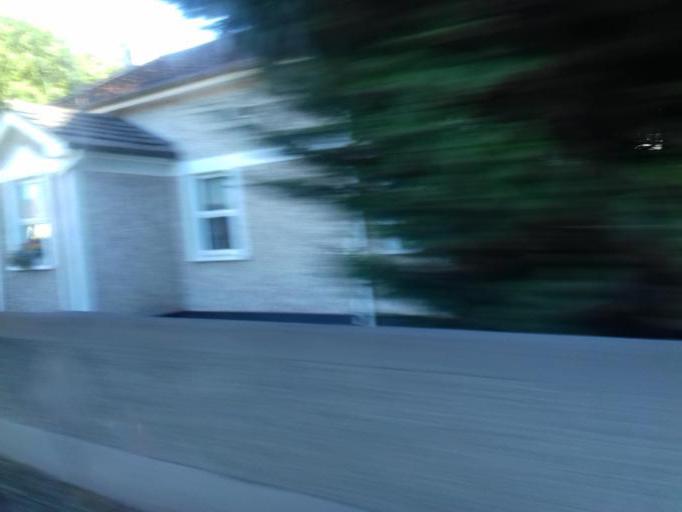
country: IE
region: Leinster
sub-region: Dublin City
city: Finglas
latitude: 53.4632
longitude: -6.3137
